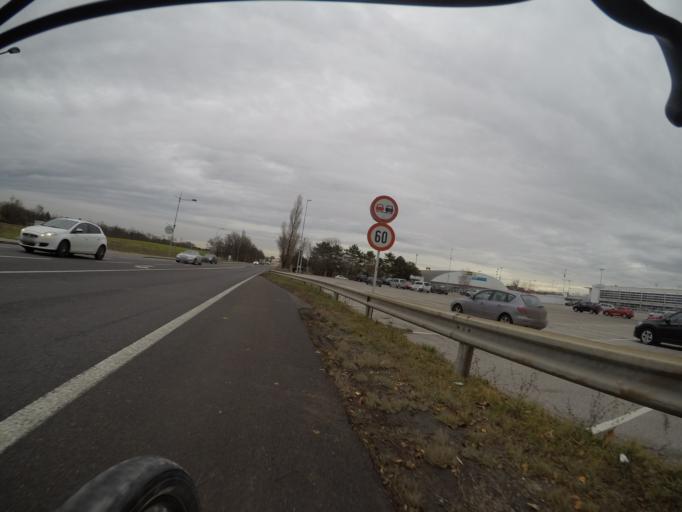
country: AT
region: Lower Austria
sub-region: Politischer Bezirk Modling
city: Wiener Neudorf
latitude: 48.0999
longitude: 16.3107
